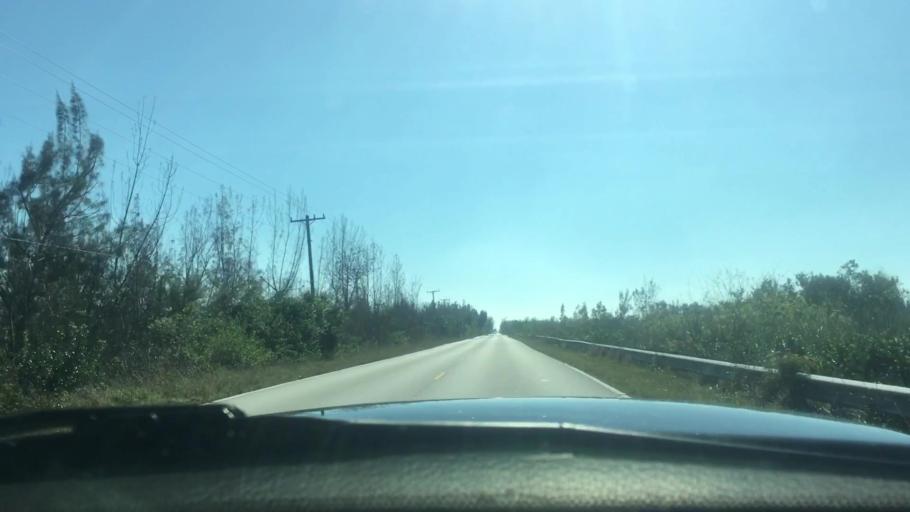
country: US
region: Florida
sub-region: Miami-Dade County
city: Florida City
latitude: 25.4261
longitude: -80.4684
